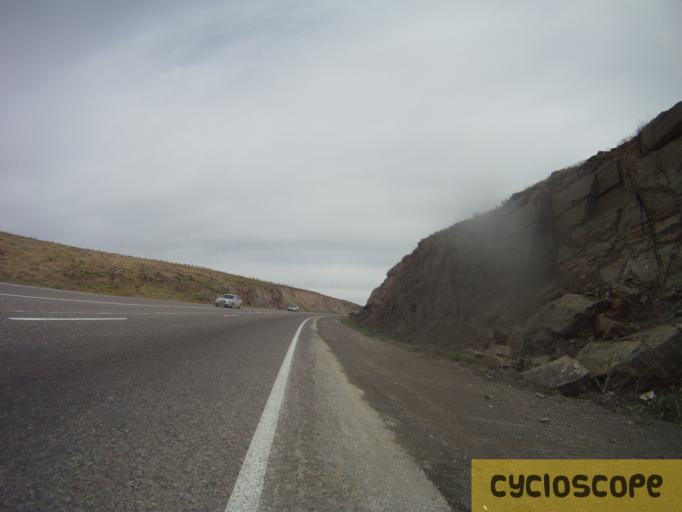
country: KZ
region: Zhambyl
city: Georgiyevka
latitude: 43.2682
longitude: 74.8349
